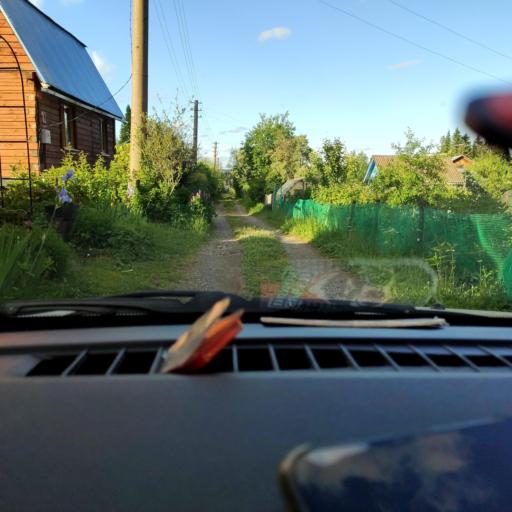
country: RU
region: Perm
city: Novyye Lyady
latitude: 58.0474
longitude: 56.6420
